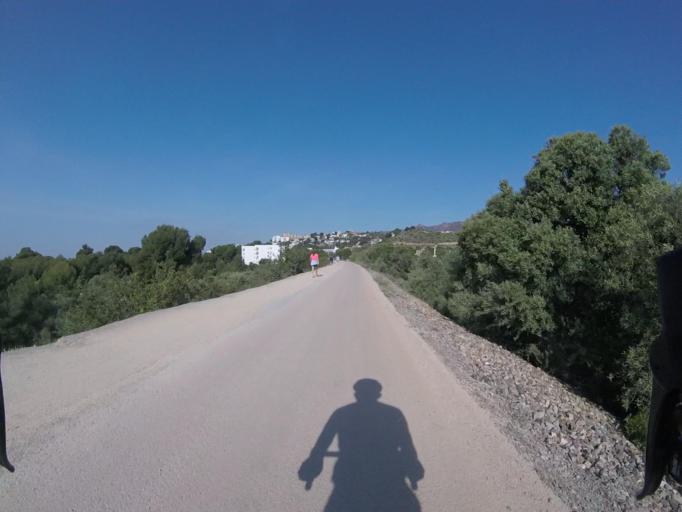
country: ES
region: Valencia
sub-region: Provincia de Castello
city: Benicassim
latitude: 40.0579
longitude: 0.1011
